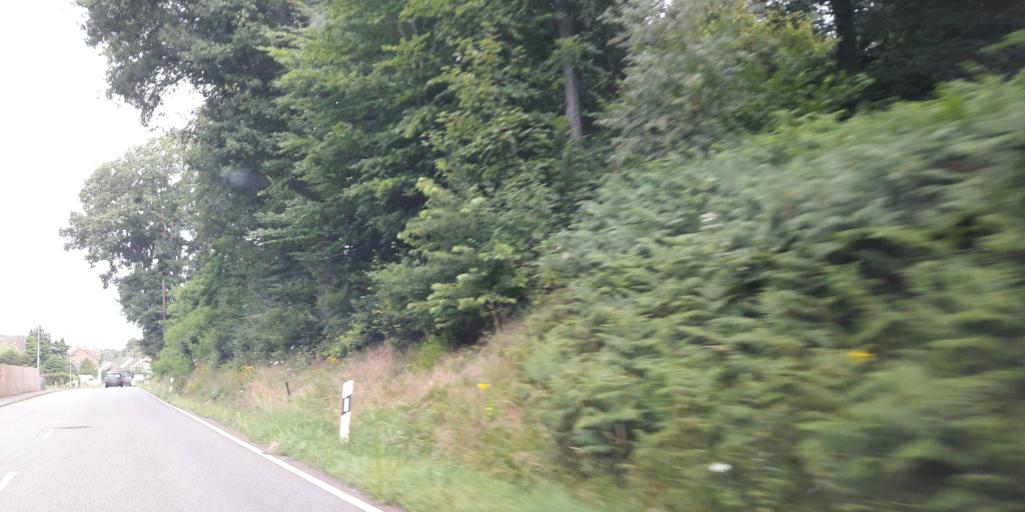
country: DE
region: Saarland
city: Puttlingen
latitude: 49.3056
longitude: 6.8639
